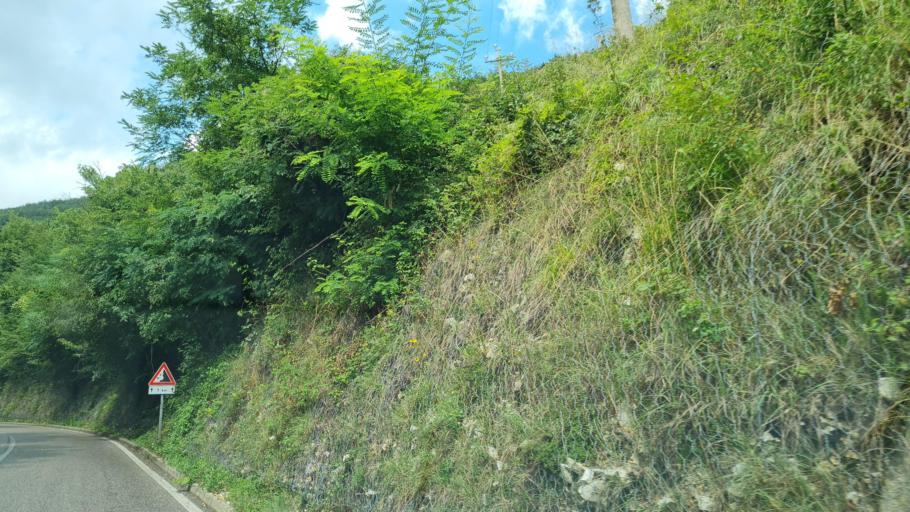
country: IT
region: Veneto
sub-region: Provincia di Vicenza
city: Marostica
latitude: 45.7855
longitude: 11.6614
